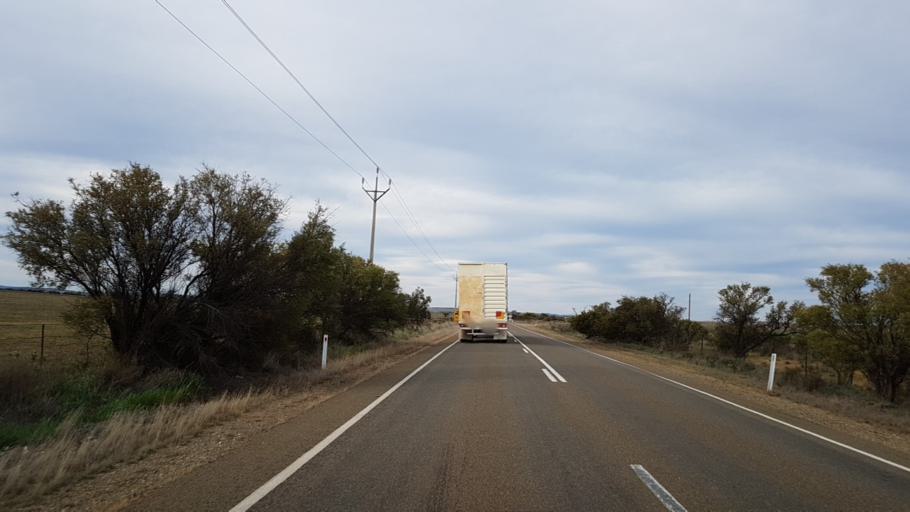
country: AU
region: South Australia
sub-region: Peterborough
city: Peterborough
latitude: -33.0169
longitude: 138.7571
